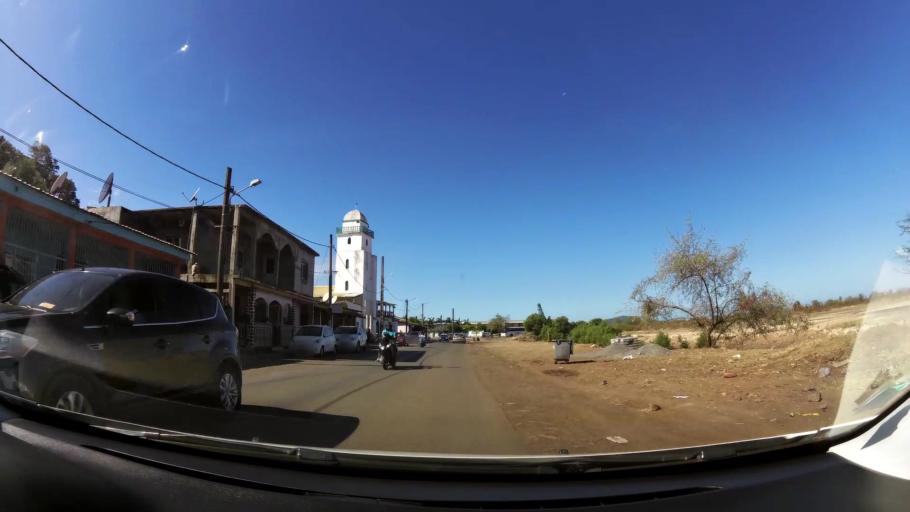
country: YT
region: Mamoudzou
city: Mamoudzou
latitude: -12.7916
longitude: 45.2193
